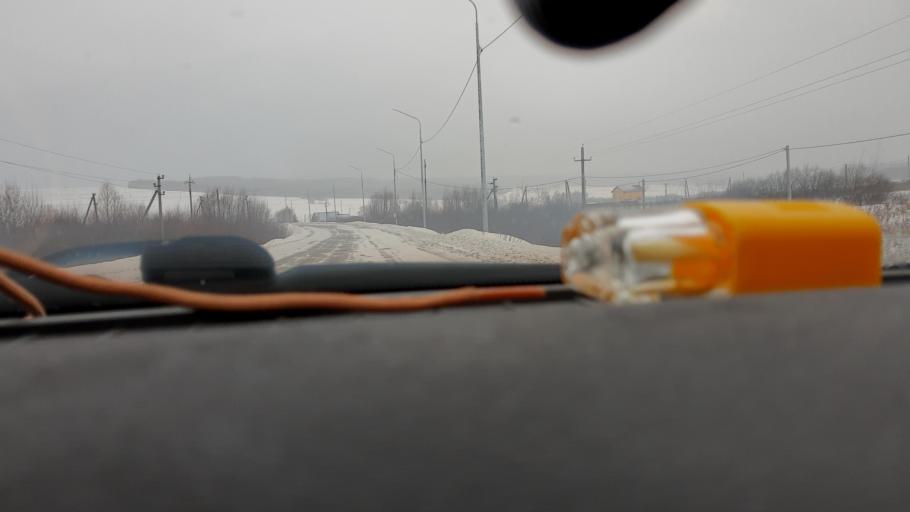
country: RU
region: Bashkortostan
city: Ulukulevo
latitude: 54.5637
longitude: 56.3397
